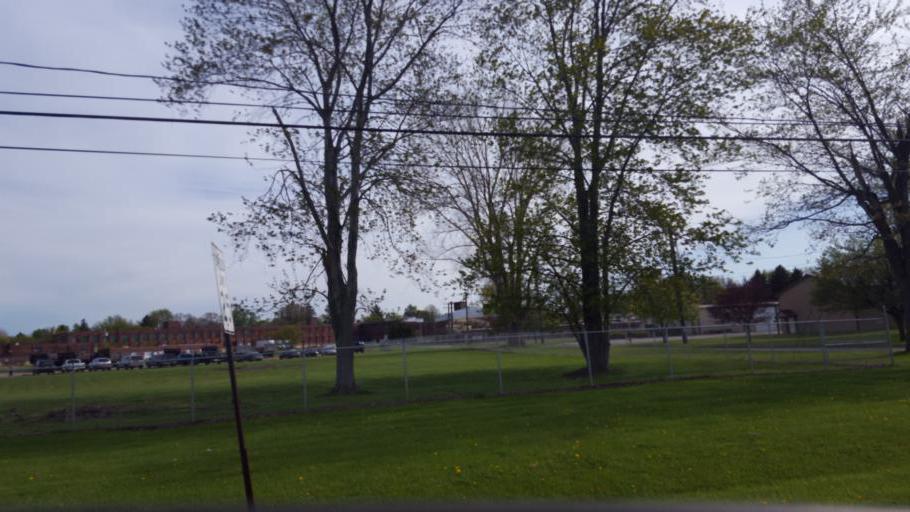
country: US
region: Ohio
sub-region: Ashtabula County
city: Geneva
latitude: 41.8122
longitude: -80.9412
